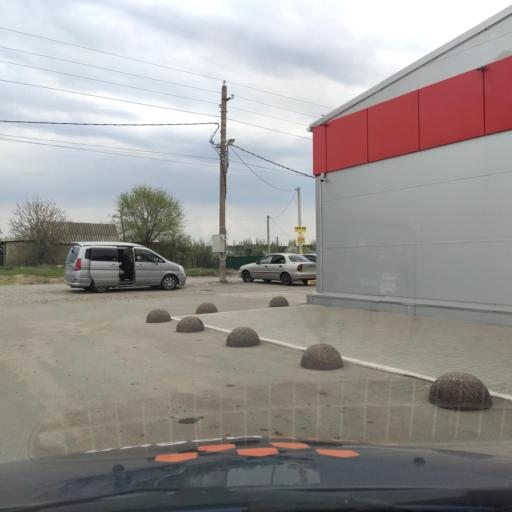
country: RU
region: Voronezj
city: Podgornoye
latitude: 51.8879
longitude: 39.1761
